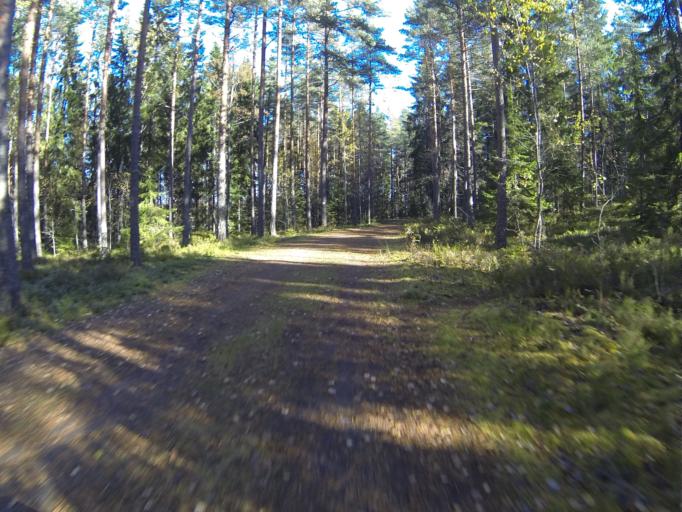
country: FI
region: Varsinais-Suomi
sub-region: Salo
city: Saerkisalo
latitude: 60.2113
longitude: 22.9262
